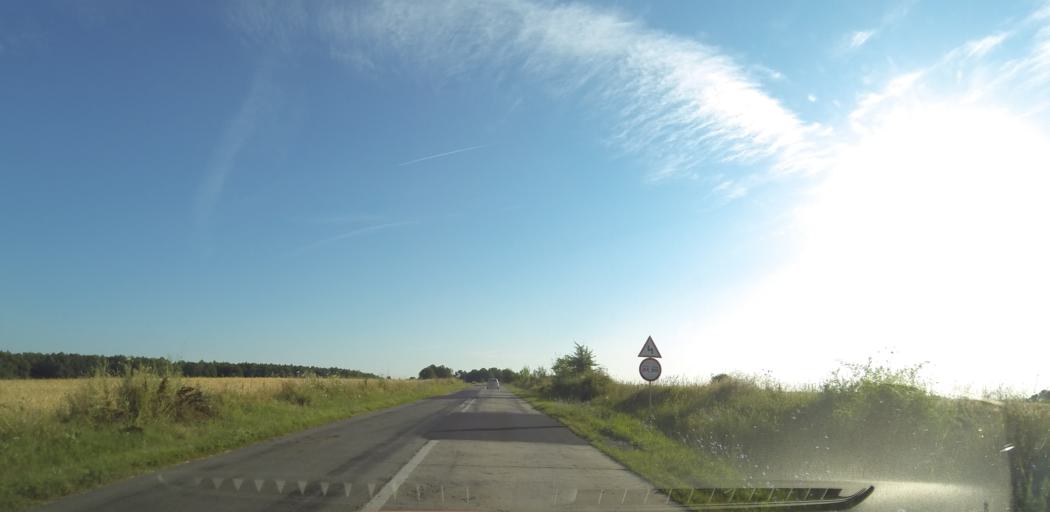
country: RO
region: Valcea
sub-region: Comuna Balcesti
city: Balcesti
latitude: 44.6019
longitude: 23.9291
